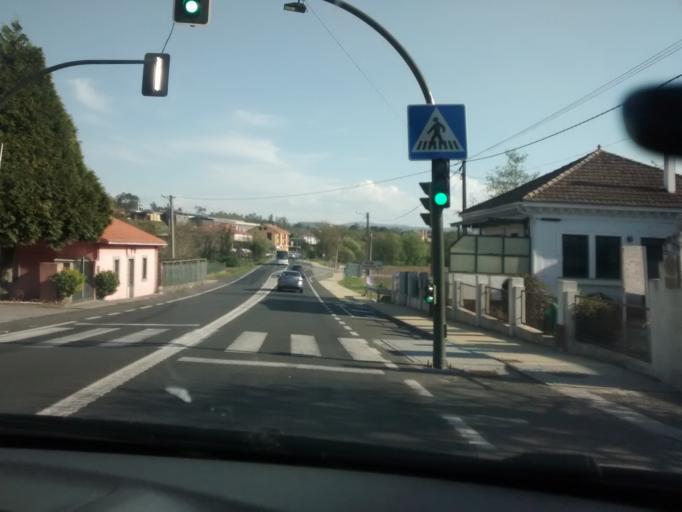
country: ES
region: Galicia
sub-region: Provincia da Coruna
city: Teo
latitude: 42.7661
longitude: -8.5486
